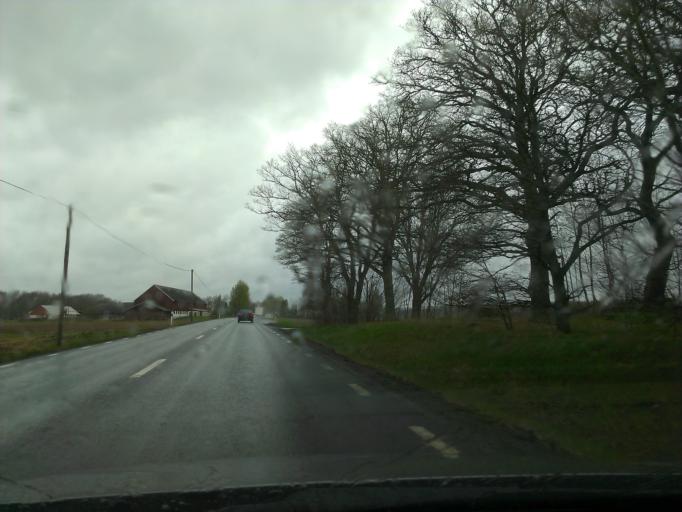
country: SE
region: Skane
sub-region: Ostra Goinge Kommun
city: Knislinge
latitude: 56.1737
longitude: 14.0966
